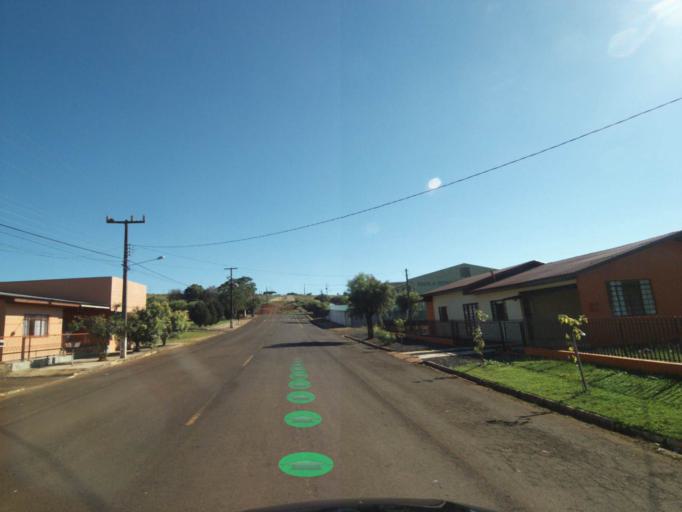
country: BR
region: Parana
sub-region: Coronel Vivida
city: Coronel Vivida
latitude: -26.1450
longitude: -52.3803
